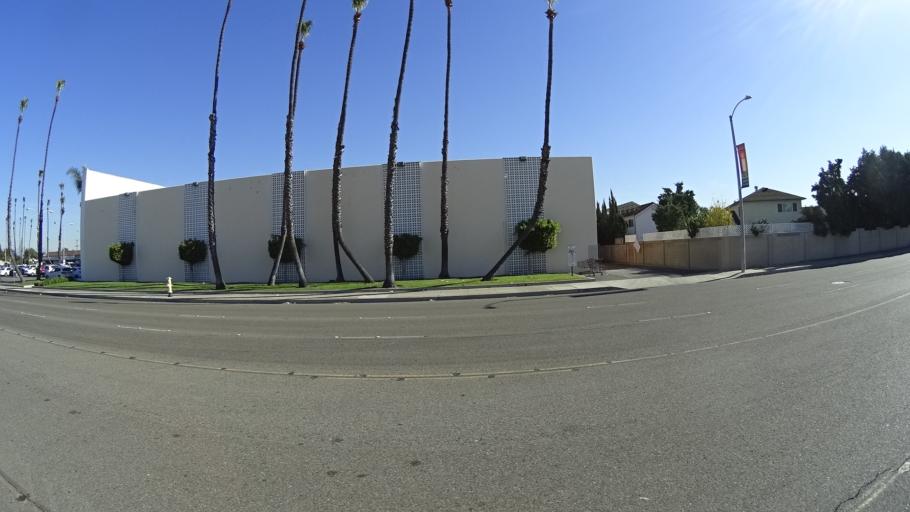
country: US
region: California
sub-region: Orange County
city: Garden Grove
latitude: 33.7506
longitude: -117.9550
